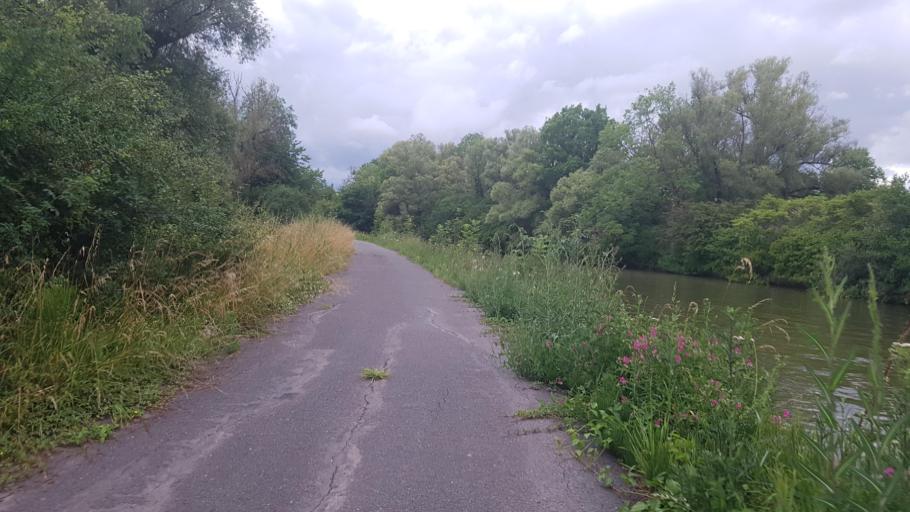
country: FR
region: Lorraine
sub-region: Departement de Meurthe-et-Moselle
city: Chanteheux
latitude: 48.6848
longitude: 6.6468
